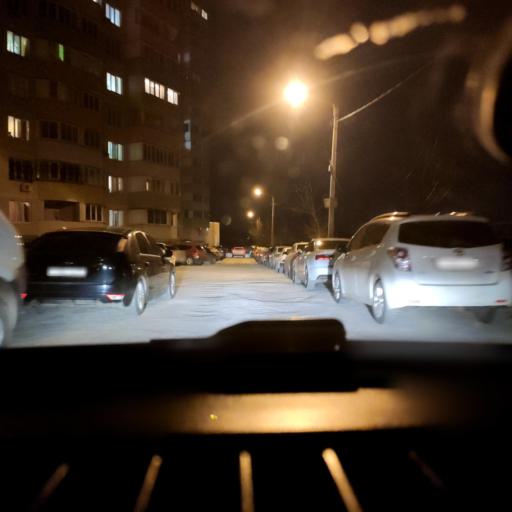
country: RU
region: Voronezj
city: Voronezh
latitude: 51.7194
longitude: 39.2142
